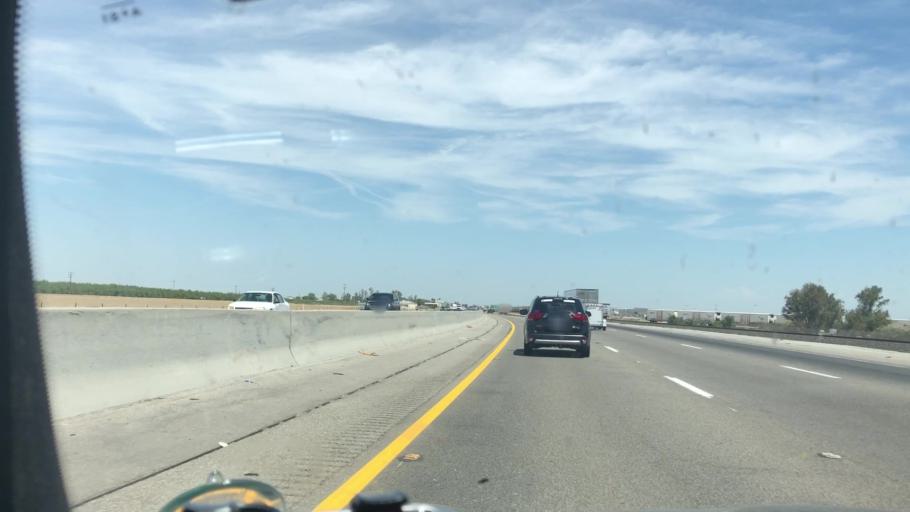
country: US
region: California
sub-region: Kern County
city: McFarland
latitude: 35.7229
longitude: -119.2376
